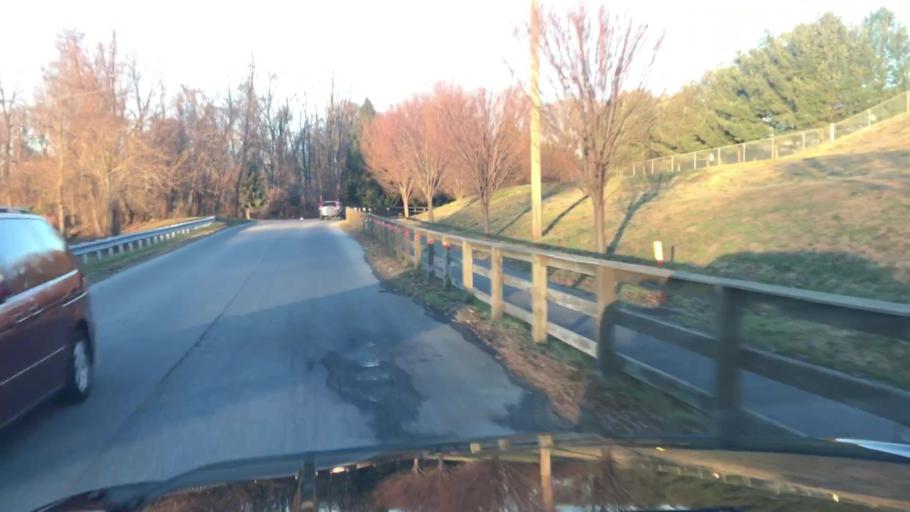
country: US
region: Pennsylvania
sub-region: Dauphin County
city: Harrisburg
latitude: 40.2804
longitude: -76.8703
